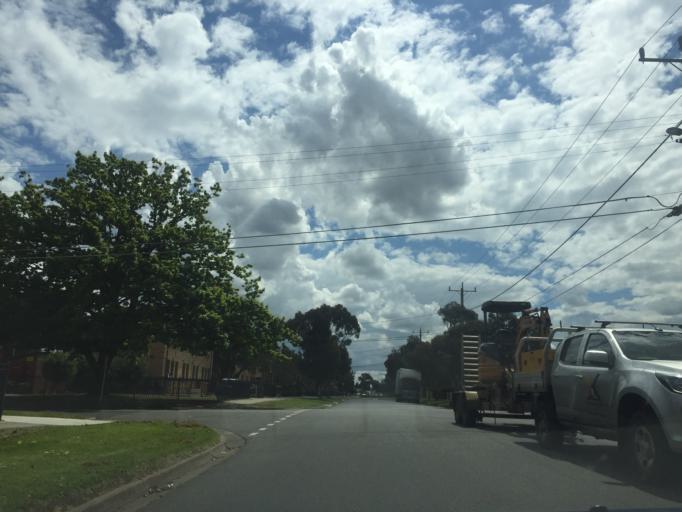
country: AU
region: Victoria
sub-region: Darebin
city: Kingsbury
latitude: -37.7144
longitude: 145.0178
